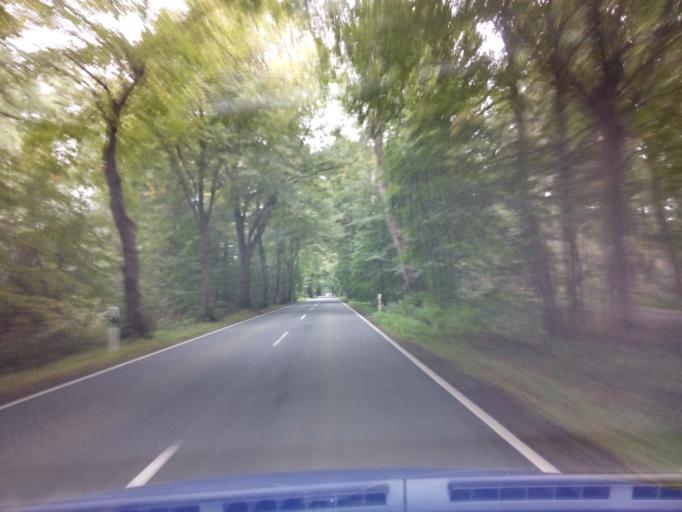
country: DE
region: Lower Saxony
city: Lubberstedt
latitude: 53.3555
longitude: 8.8268
